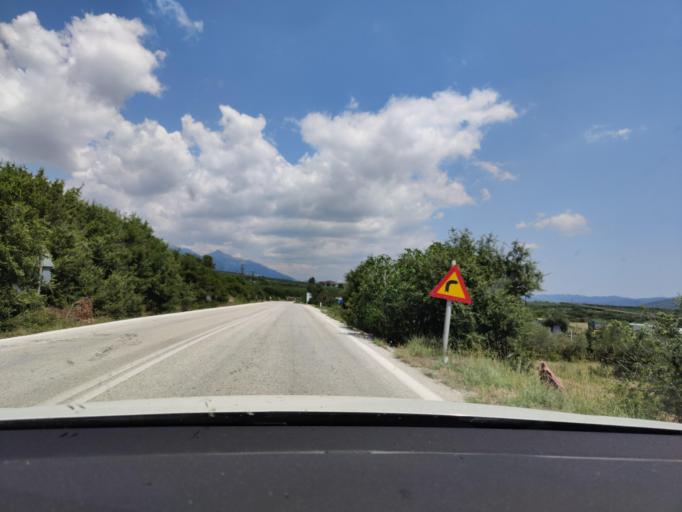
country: GR
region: East Macedonia and Thrace
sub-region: Nomos Kavalas
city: Paralia Ofryniou
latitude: 40.8082
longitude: 23.9820
